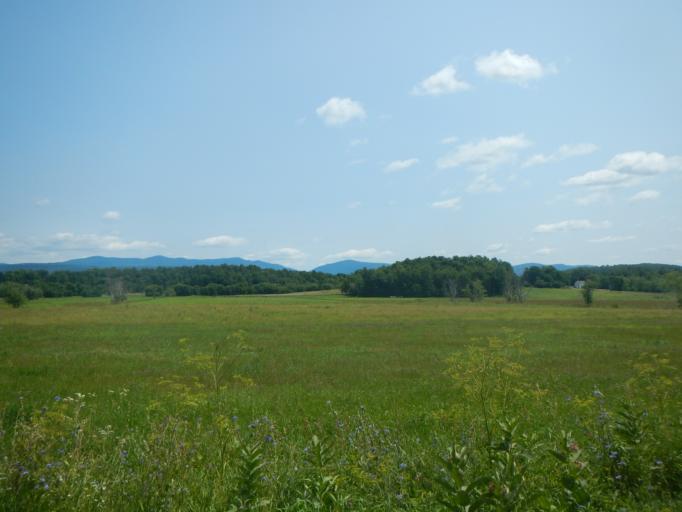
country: US
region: Vermont
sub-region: Rutland County
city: Brandon
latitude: 43.8588
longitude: -73.1475
